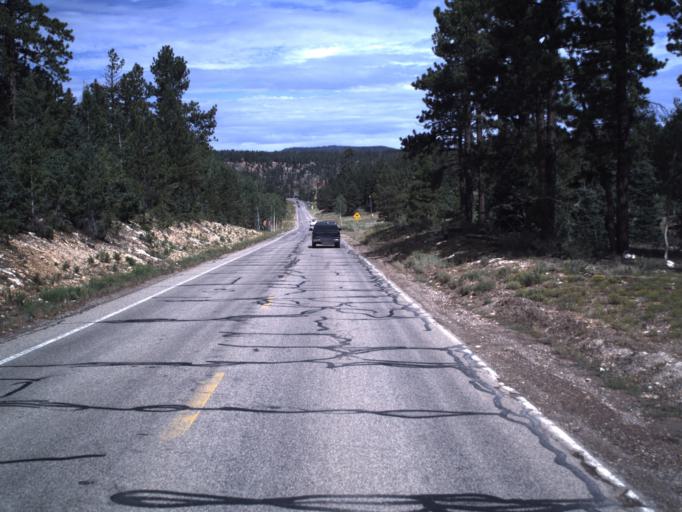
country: US
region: Utah
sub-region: Iron County
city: Parowan
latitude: 37.5199
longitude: -112.6506
